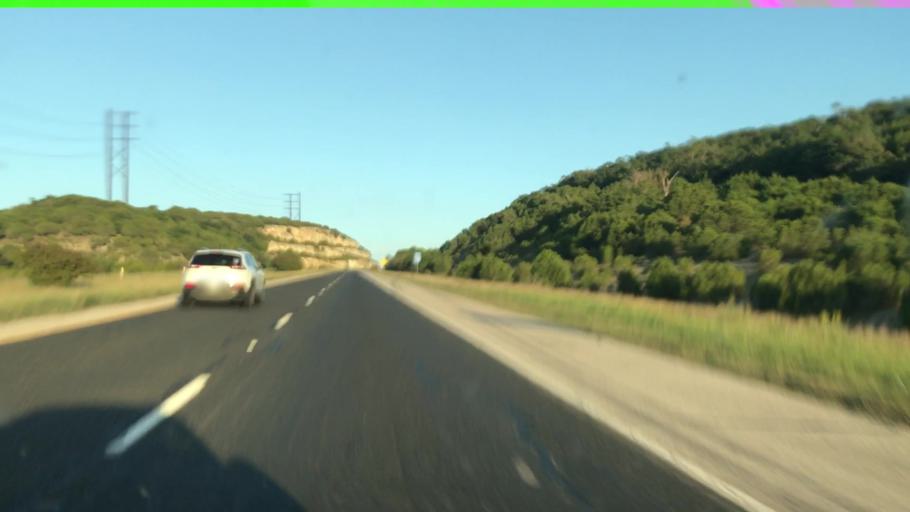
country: US
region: Texas
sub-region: Kerr County
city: Kerrville
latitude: 30.0703
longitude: -99.1053
